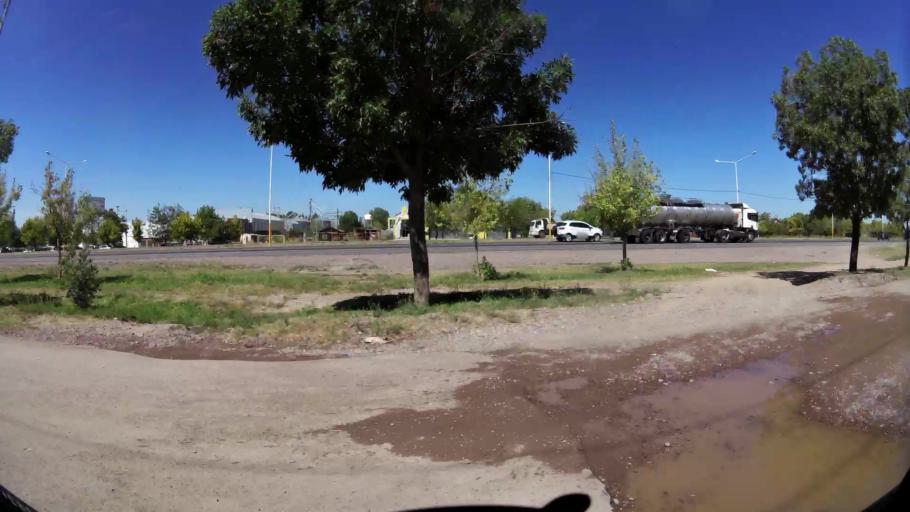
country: AR
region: Mendoza
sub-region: Departamento de Godoy Cruz
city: Godoy Cruz
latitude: -32.9781
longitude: -68.8475
